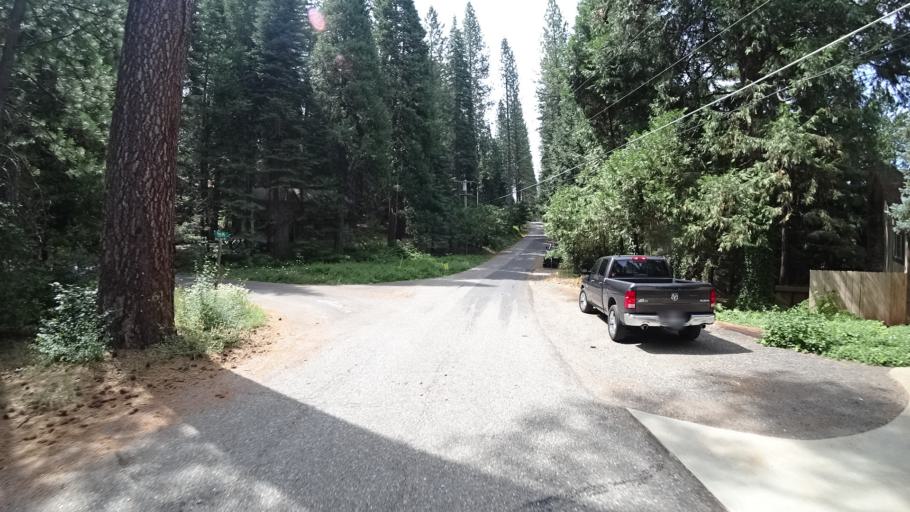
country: US
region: California
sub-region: Calaveras County
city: Arnold
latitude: 38.2464
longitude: -120.3578
